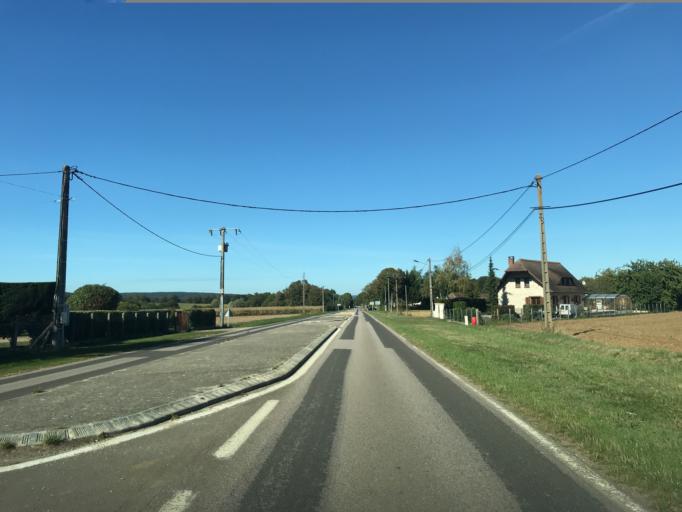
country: FR
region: Haute-Normandie
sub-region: Departement de l'Eure
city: Saint-Pierre-du-Vauvray
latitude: 49.2367
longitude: 1.2114
